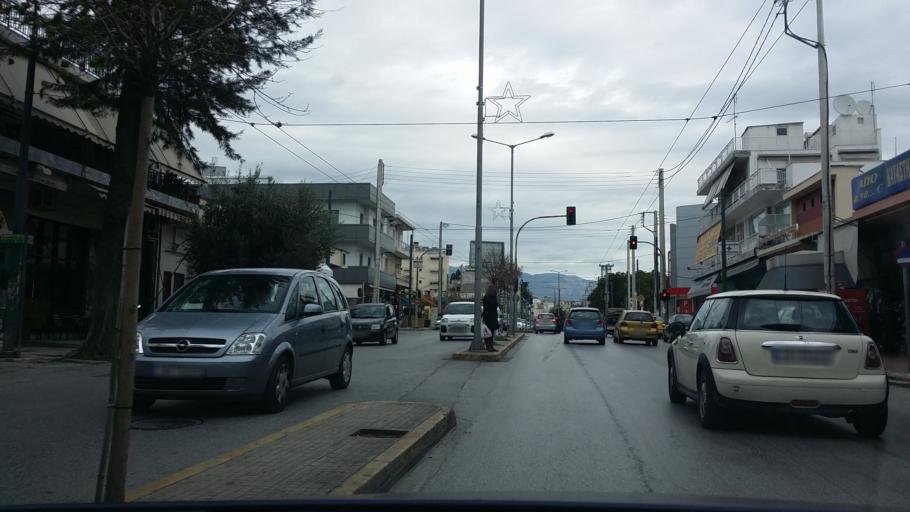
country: GR
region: Attica
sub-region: Nomarchia Athinas
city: Peristeri
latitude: 38.0214
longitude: 23.6940
